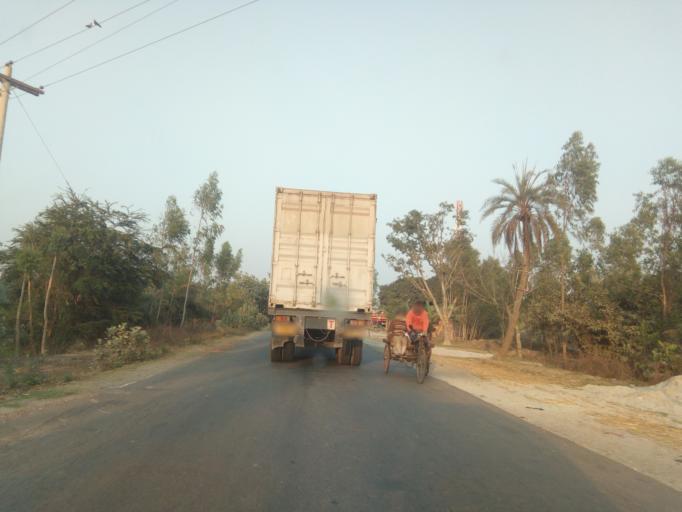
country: BD
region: Rajshahi
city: Bogra
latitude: 24.5533
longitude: 89.1938
